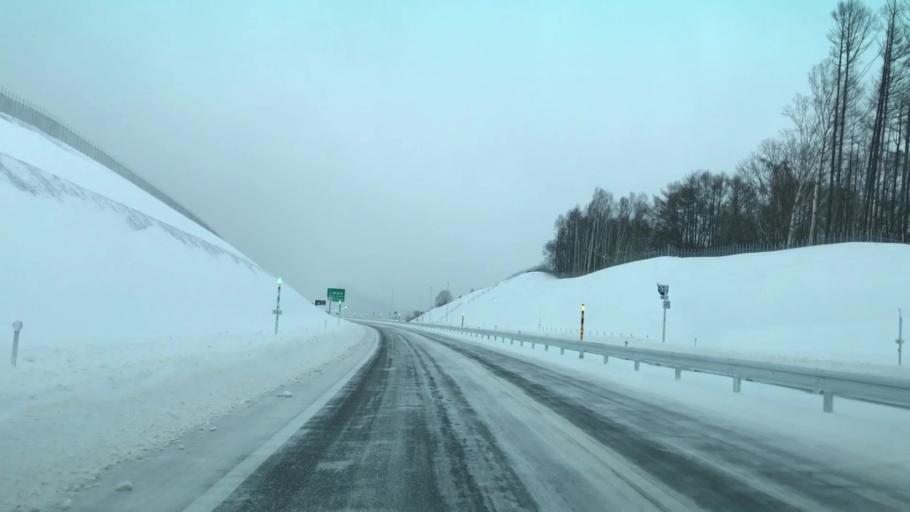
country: JP
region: Hokkaido
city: Otaru
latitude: 43.1998
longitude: 140.9382
